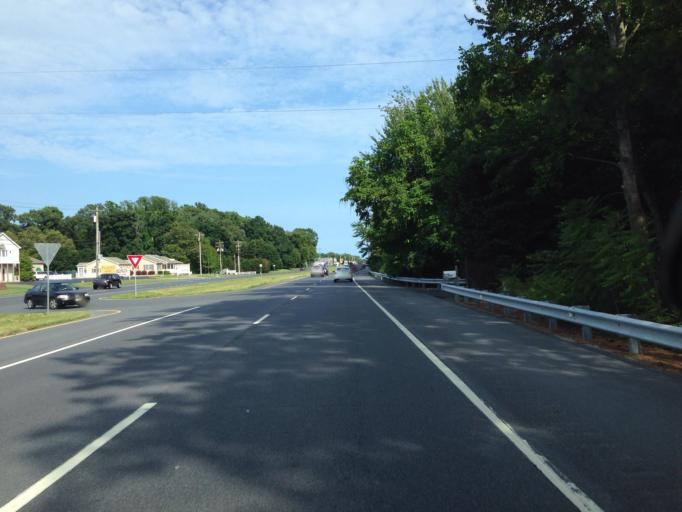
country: US
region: Delaware
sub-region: Sussex County
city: Lewes
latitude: 38.7598
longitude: -75.2022
